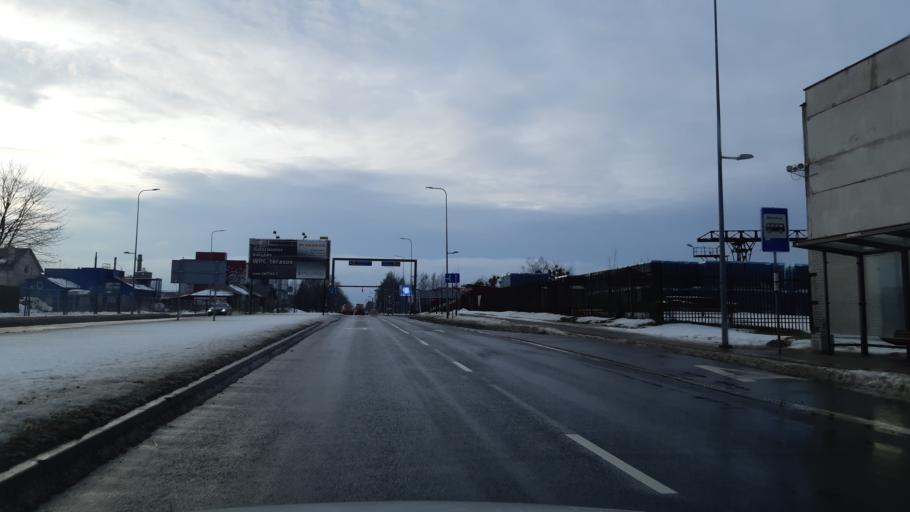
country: LT
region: Kauno apskritis
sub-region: Kaunas
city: Aleksotas
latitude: 54.8751
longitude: 23.8947
